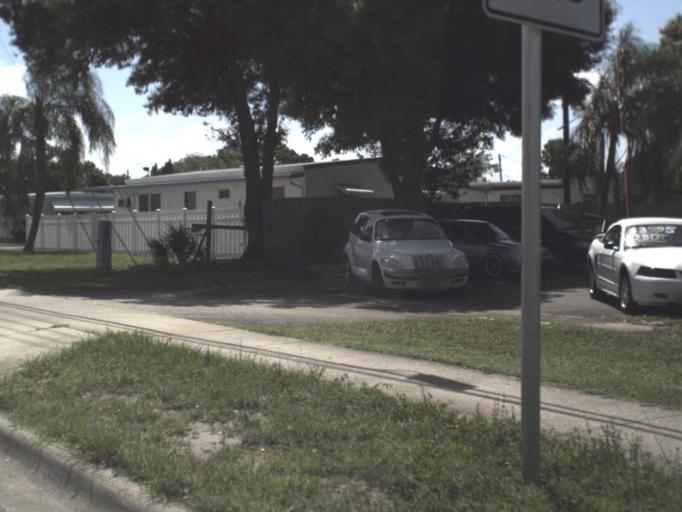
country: US
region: Florida
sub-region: Pinellas County
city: South Highpoint
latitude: 27.9162
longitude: -82.7340
